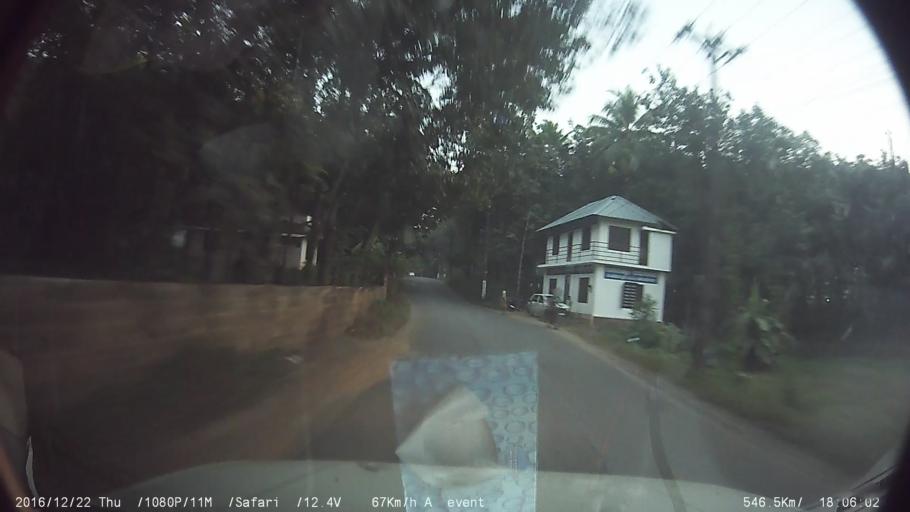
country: IN
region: Kerala
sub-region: Kottayam
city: Palackattumala
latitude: 9.8231
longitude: 76.6080
